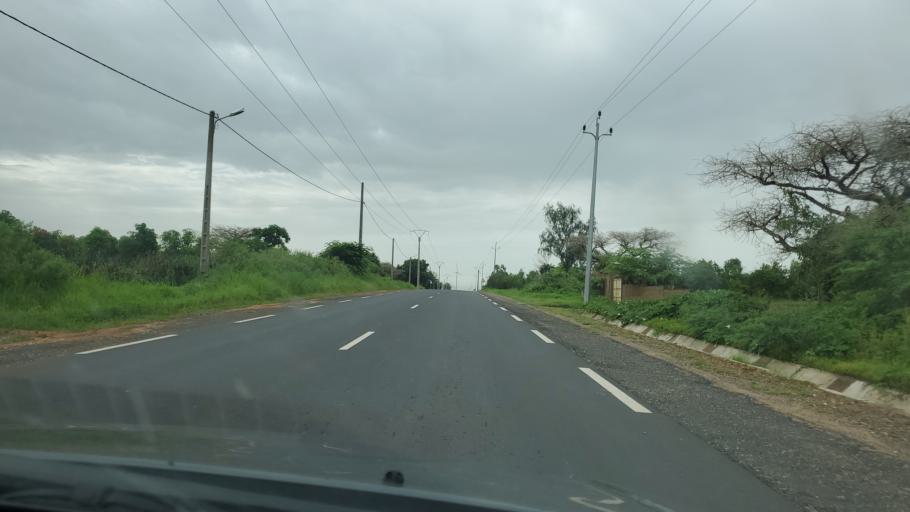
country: SN
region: Thies
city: Kayar
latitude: 15.1026
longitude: -16.9137
